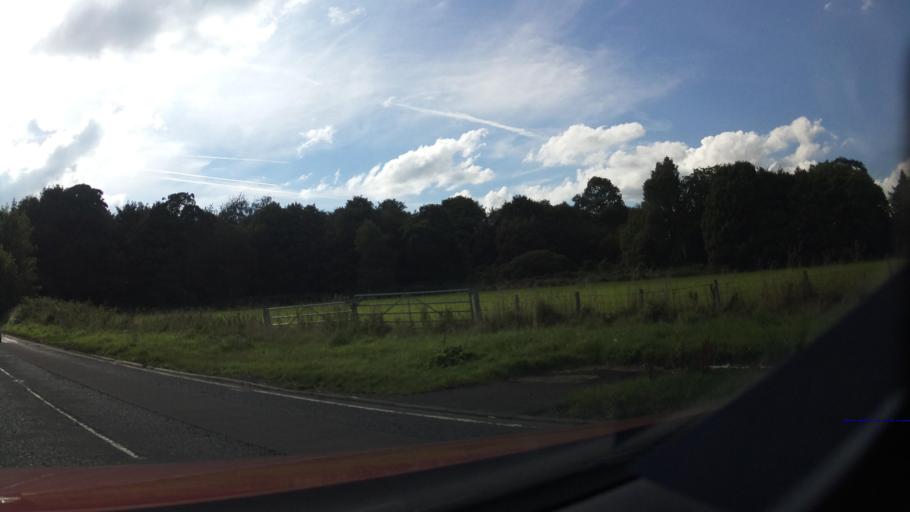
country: GB
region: Scotland
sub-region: Stirling
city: Cowie
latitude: 56.0466
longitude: -3.8574
